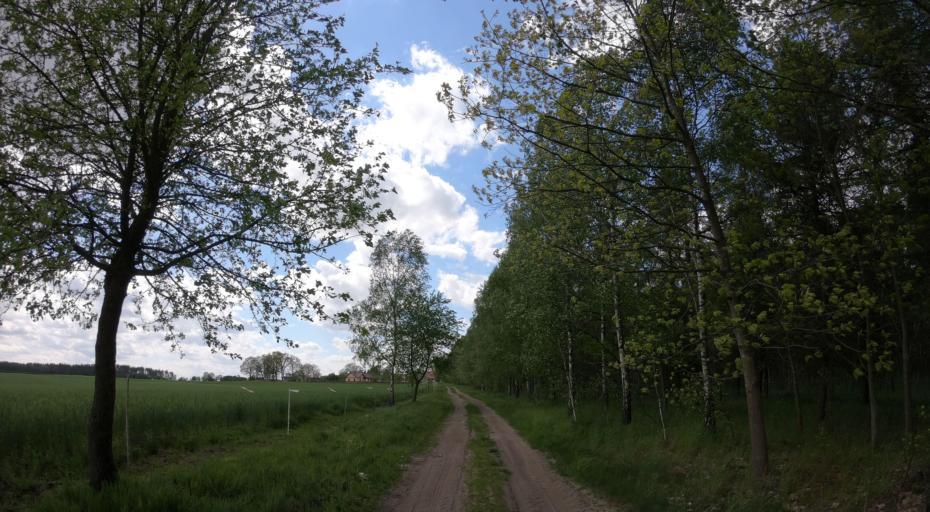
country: PL
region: West Pomeranian Voivodeship
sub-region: Powiat lobeski
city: Lobez
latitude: 53.6048
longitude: 15.6876
